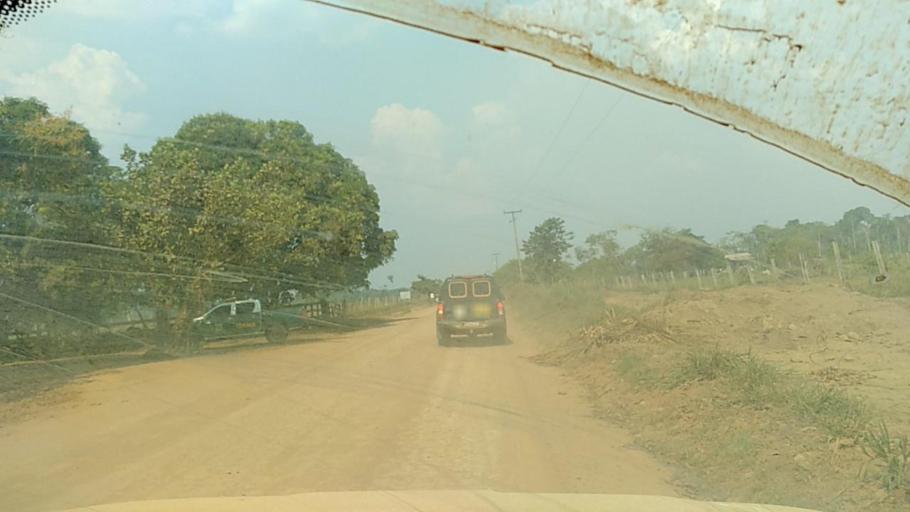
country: BR
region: Rondonia
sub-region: Porto Velho
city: Porto Velho
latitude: -8.6828
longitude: -63.2044
